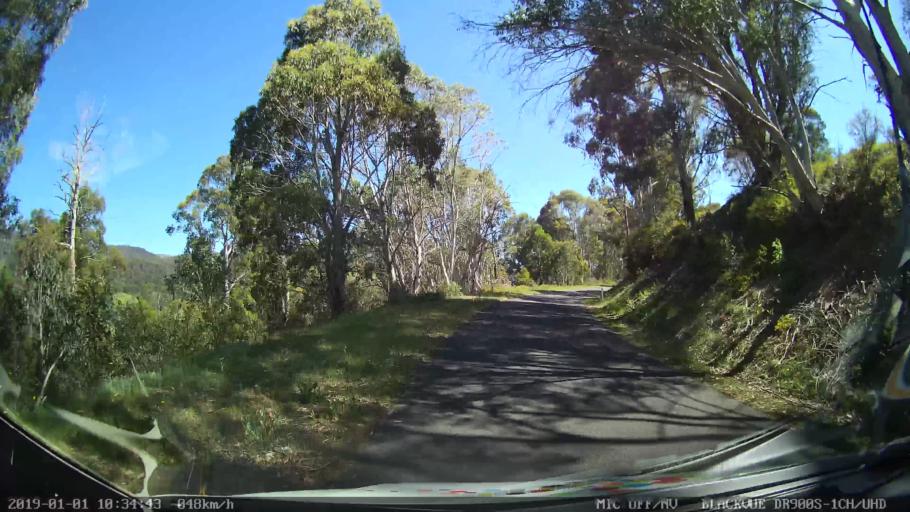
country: AU
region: New South Wales
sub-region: Snowy River
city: Jindabyne
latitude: -36.0485
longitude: 148.2844
